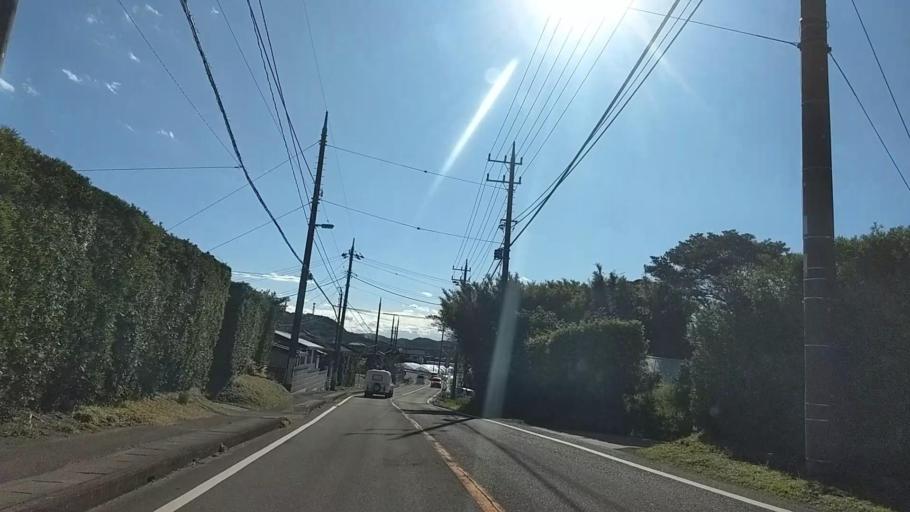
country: JP
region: Chiba
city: Tateyama
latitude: 34.9435
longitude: 139.8369
